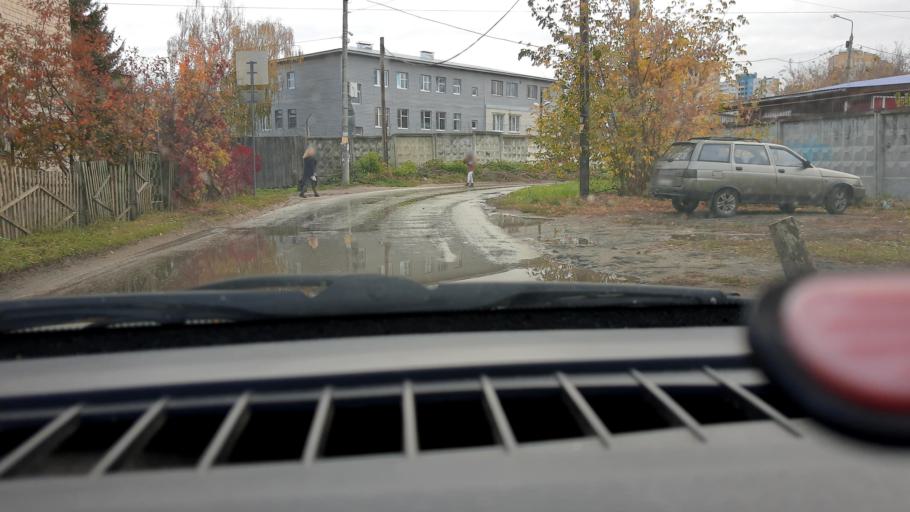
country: RU
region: Nizjnij Novgorod
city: Gorbatovka
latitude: 56.2404
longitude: 43.8371
